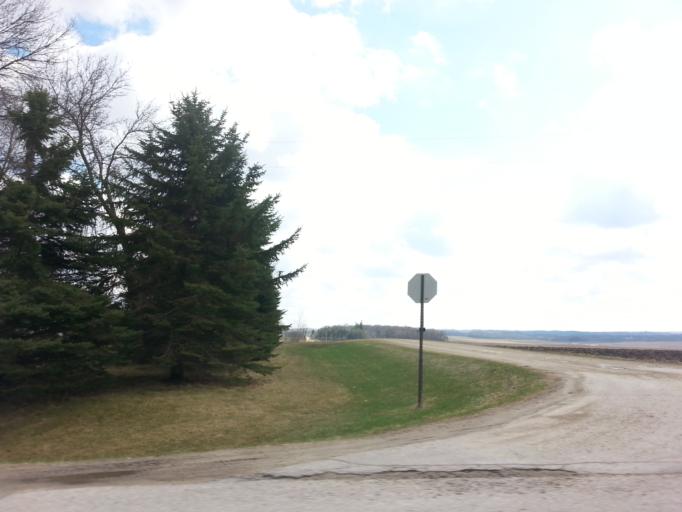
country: US
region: Minnesota
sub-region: Dodge County
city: Mantorville
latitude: 44.0942
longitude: -92.6932
